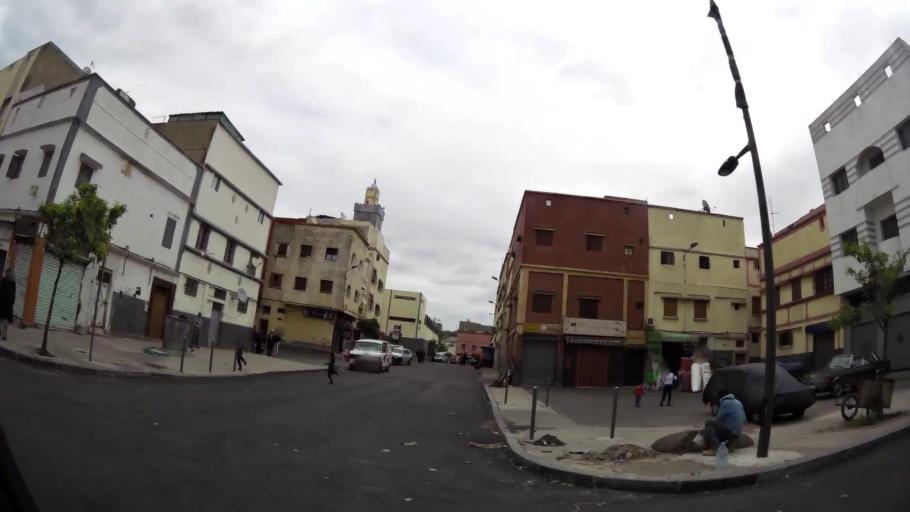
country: MA
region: Grand Casablanca
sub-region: Casablanca
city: Casablanca
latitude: 33.5831
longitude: -7.5622
